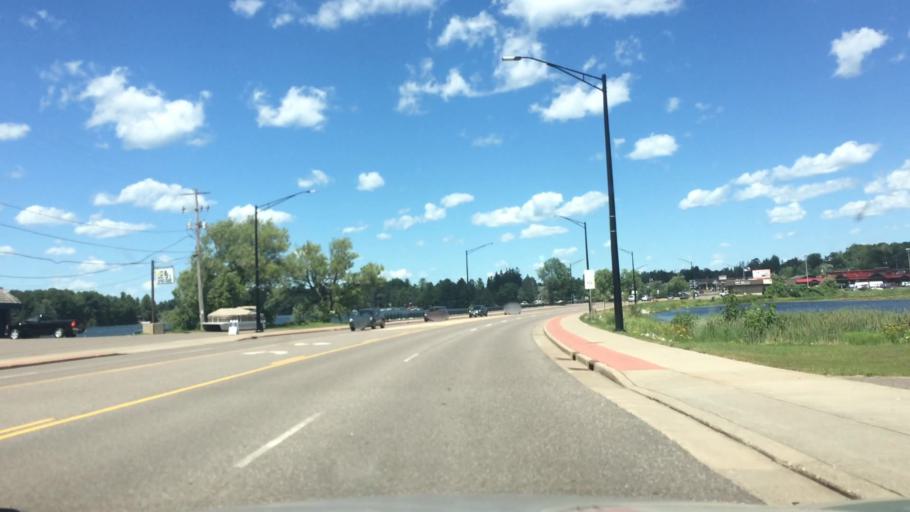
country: US
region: Wisconsin
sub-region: Vilas County
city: Lac du Flambeau
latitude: 45.8739
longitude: -89.7069
